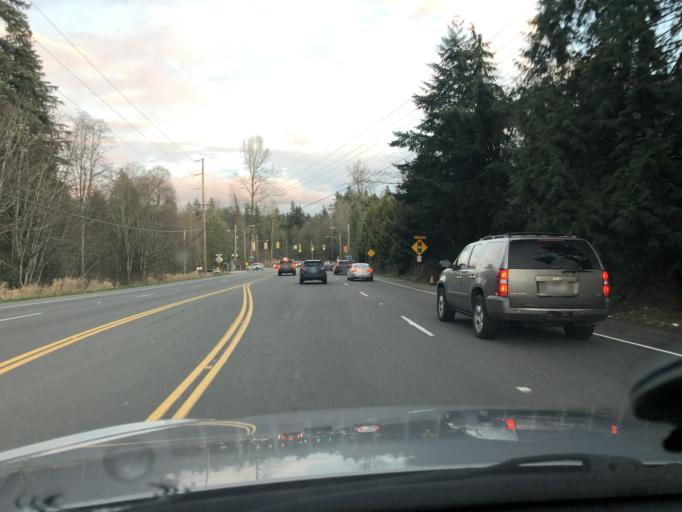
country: US
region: Washington
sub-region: King County
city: Lakeland North
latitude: 47.3146
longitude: -122.2824
